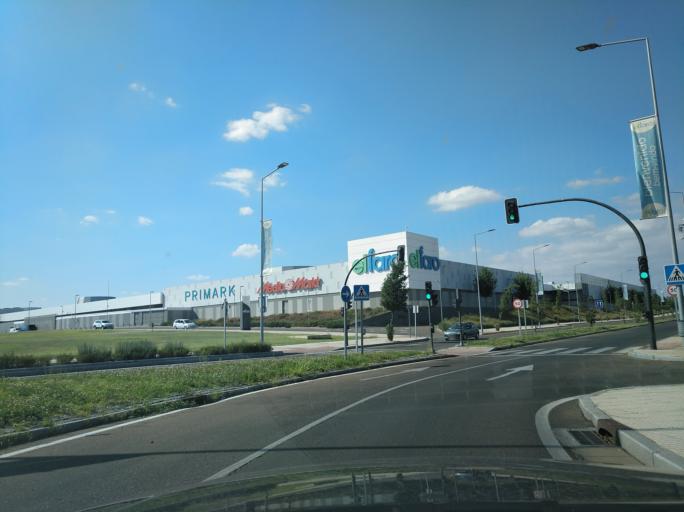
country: ES
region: Extremadura
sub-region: Provincia de Badajoz
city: Badajoz
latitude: 38.8827
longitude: -7.0196
